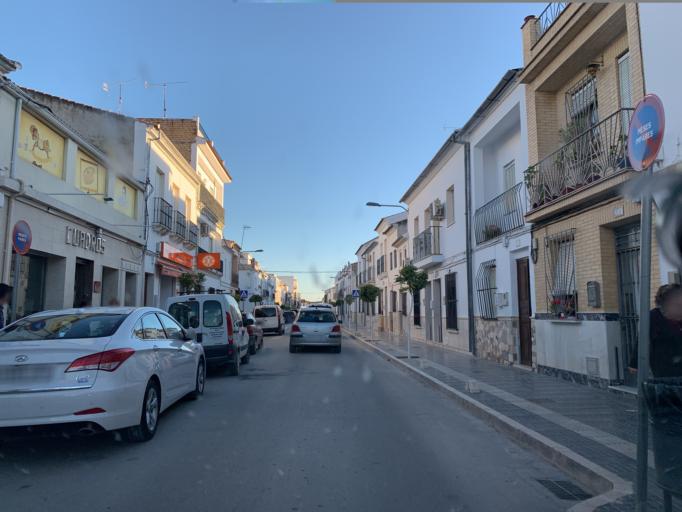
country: ES
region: Andalusia
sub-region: Provincia de Sevilla
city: Pedrera
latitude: 37.2256
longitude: -4.8934
